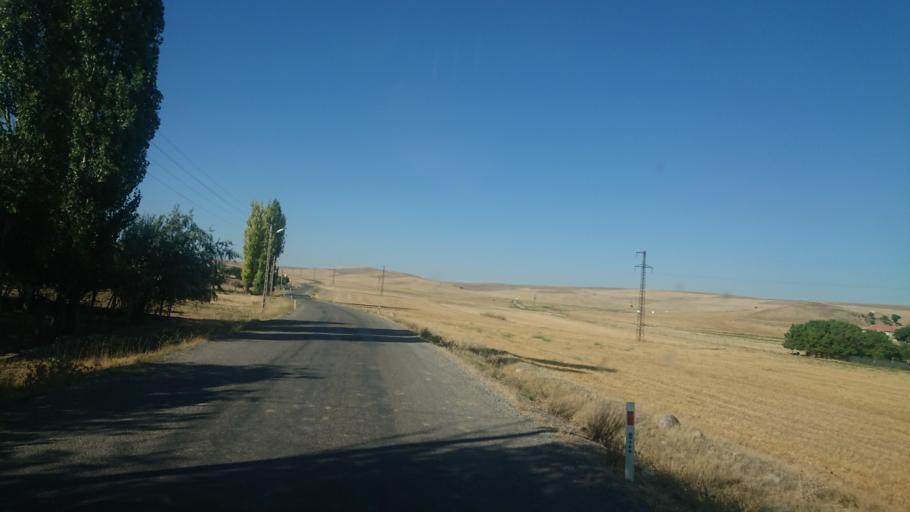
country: TR
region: Aksaray
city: Agacoren
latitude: 38.7734
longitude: 33.7065
